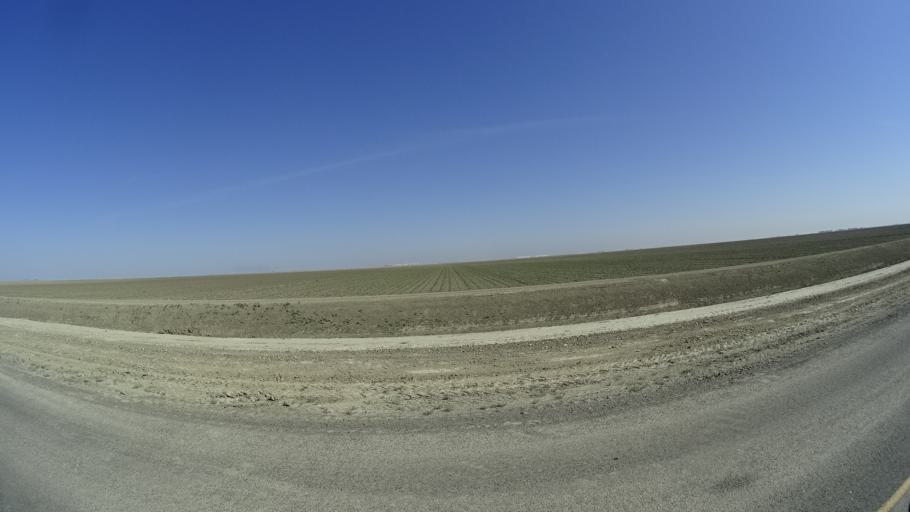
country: US
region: California
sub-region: Tulare County
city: Alpaugh
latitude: 35.8913
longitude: -119.5643
